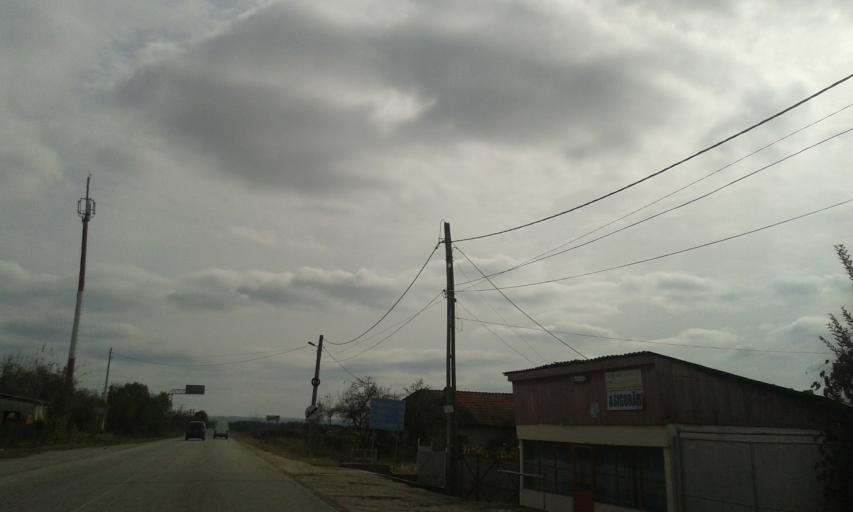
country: RO
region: Gorj
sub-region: Comuna Scoarta
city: Scoarta
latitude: 45.0164
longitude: 23.4677
